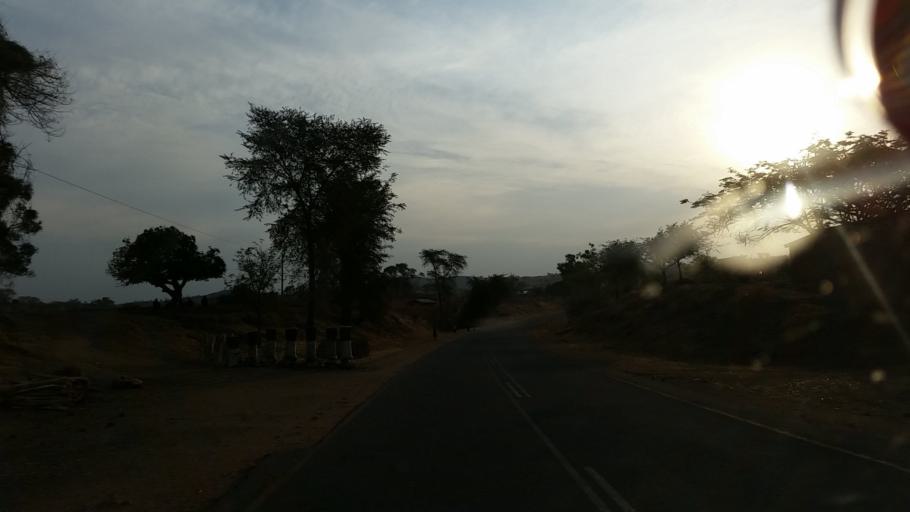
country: MW
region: Central Region
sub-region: Salima District
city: Salima
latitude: -13.7632
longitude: 34.2129
